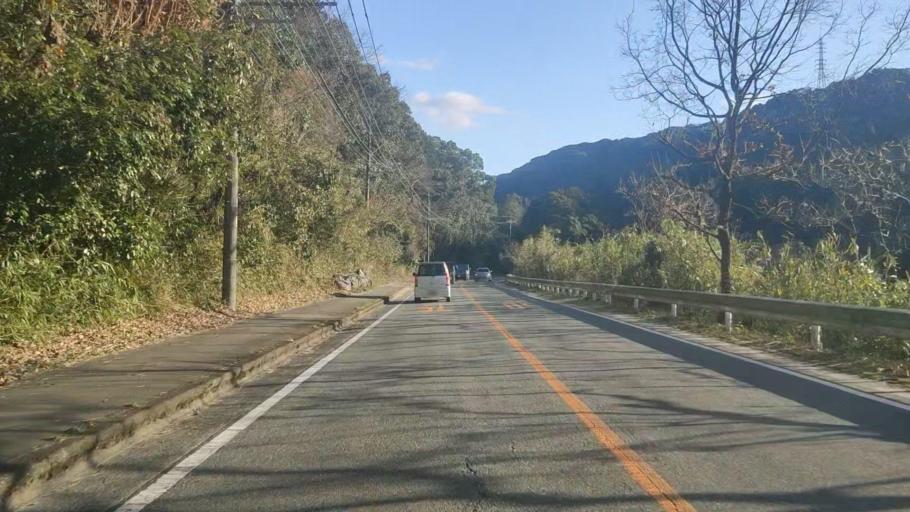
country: JP
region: Saga Prefecture
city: Saga-shi
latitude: 33.3353
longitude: 130.2618
